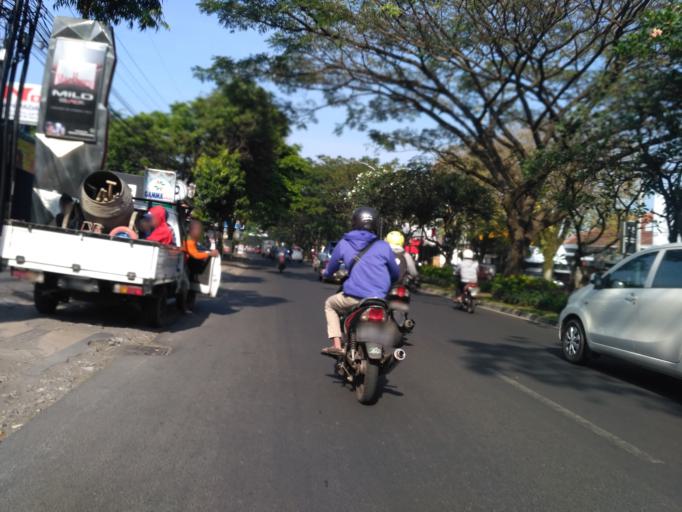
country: ID
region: East Java
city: Malang
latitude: -7.9453
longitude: 112.6190
